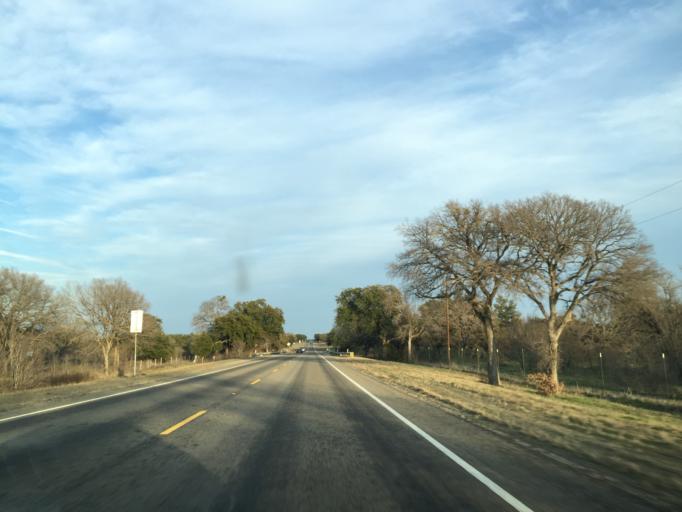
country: US
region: Texas
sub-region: Llano County
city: Buchanan Dam
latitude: 30.7328
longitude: -98.4885
